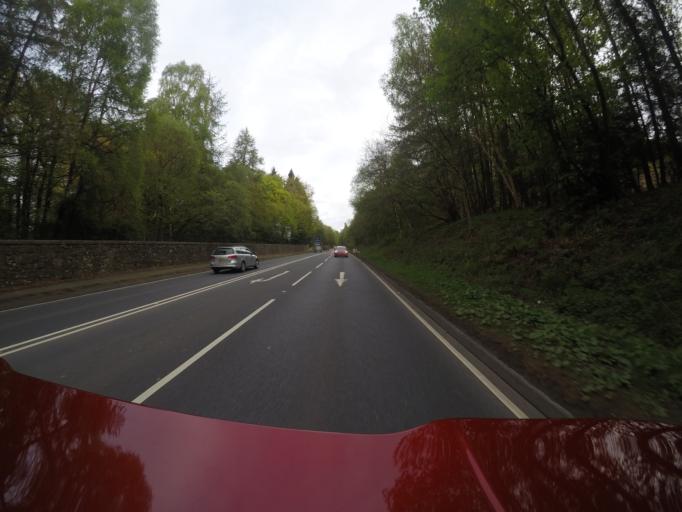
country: GB
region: Scotland
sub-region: West Dunbartonshire
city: Balloch
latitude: 56.0127
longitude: -4.6109
